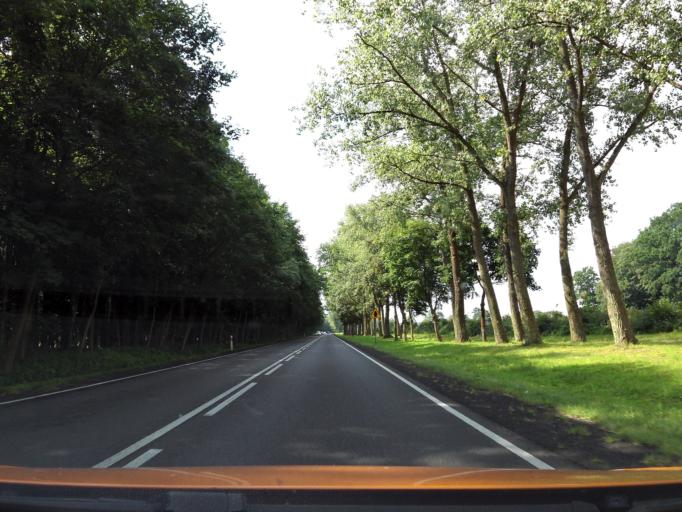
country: PL
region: West Pomeranian Voivodeship
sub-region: Powiat gryficki
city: Ploty
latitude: 53.8380
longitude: 15.3038
